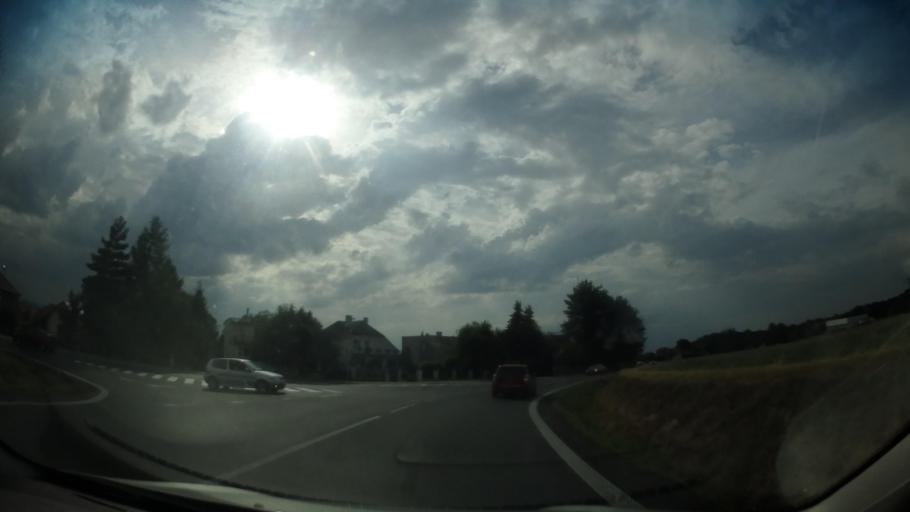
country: CZ
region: Pardubicky
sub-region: Okres Chrudim
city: Tremosnice
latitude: 49.8761
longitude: 15.5747
